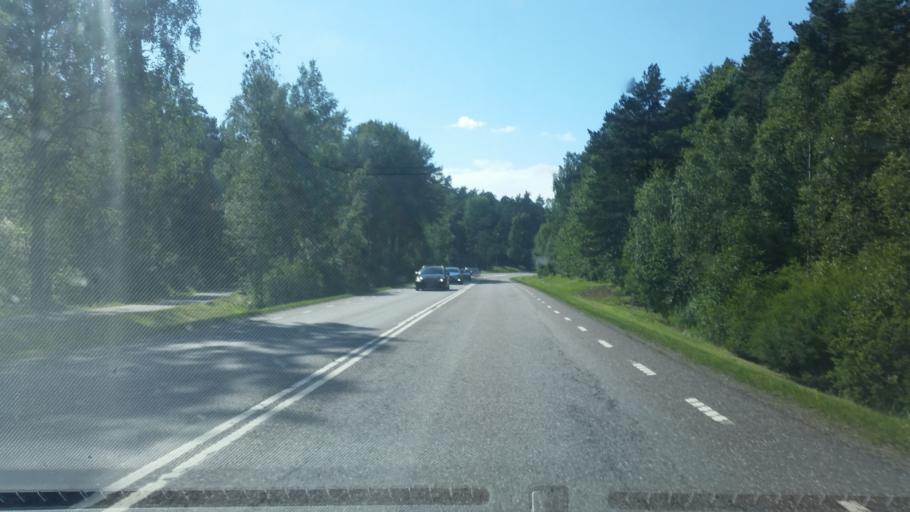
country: SE
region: Vaestra Goetaland
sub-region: Partille Kommun
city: Furulund
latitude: 57.7259
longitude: 12.1237
